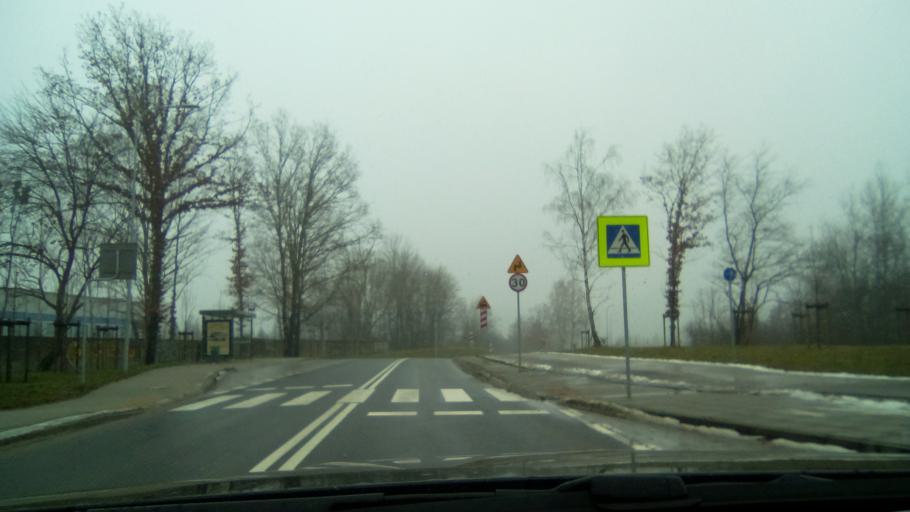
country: PL
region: Greater Poland Voivodeship
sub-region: Powiat poznanski
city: Swarzedz
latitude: 52.3889
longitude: 17.0092
